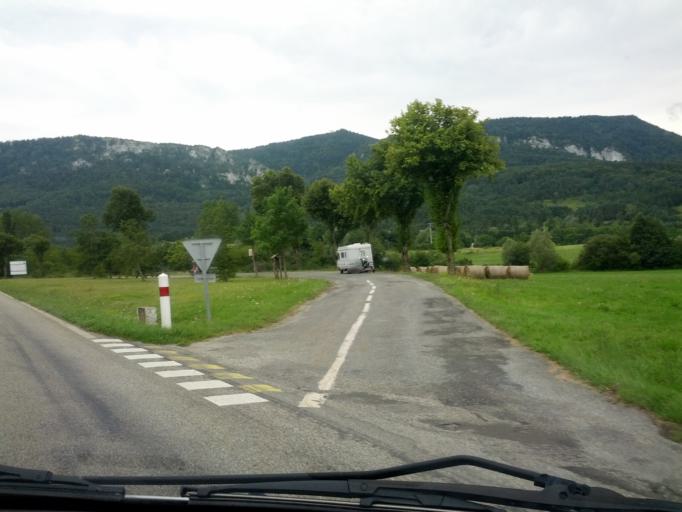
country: FR
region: Languedoc-Roussillon
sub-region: Departement de l'Aude
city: Quillan
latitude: 42.8984
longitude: 2.1097
